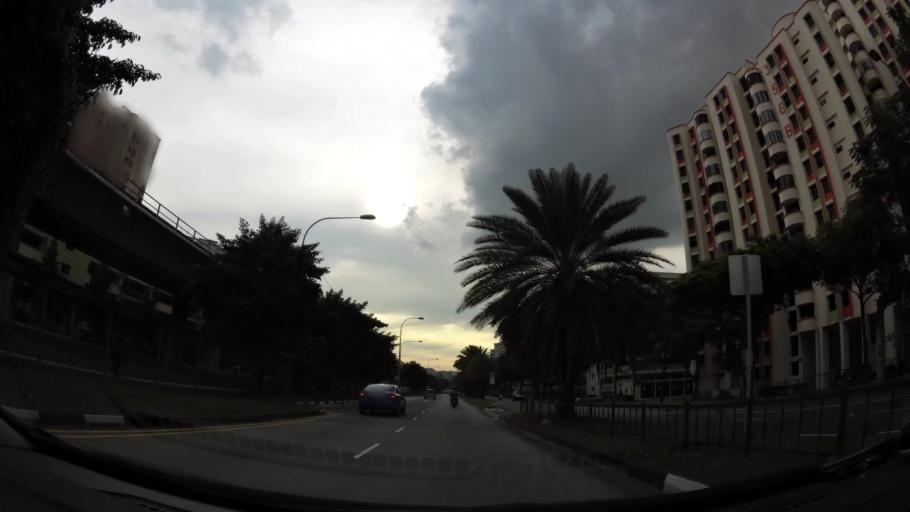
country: MY
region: Johor
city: Johor Bahru
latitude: 1.4489
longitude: 103.8177
